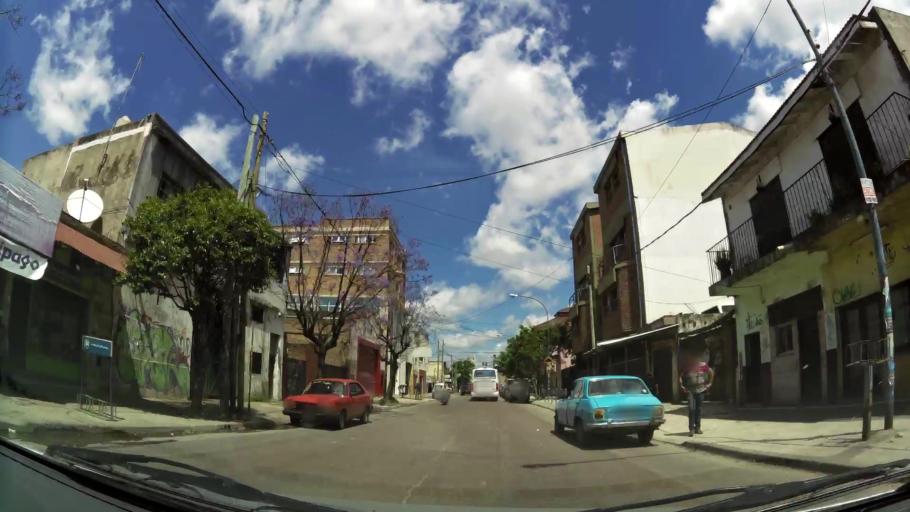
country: AR
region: Buenos Aires
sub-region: Partido de Lanus
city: Lanus
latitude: -34.6968
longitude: -58.4257
